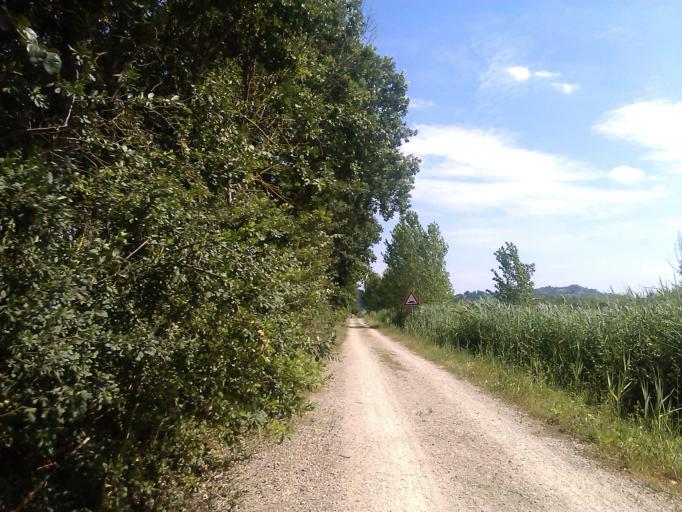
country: IT
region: Tuscany
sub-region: Provincia di Siena
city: Chiusi
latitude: 43.0617
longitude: 11.9329
